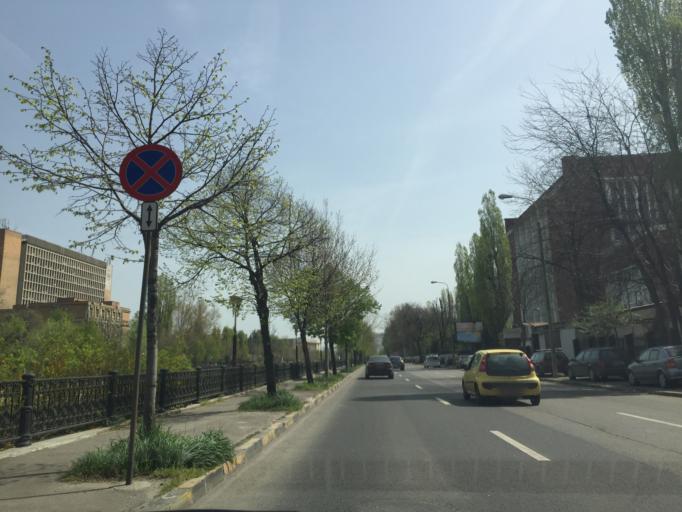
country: RO
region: Bucuresti
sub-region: Municipiul Bucuresti
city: Bucuresti
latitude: 44.4418
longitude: 26.0636
